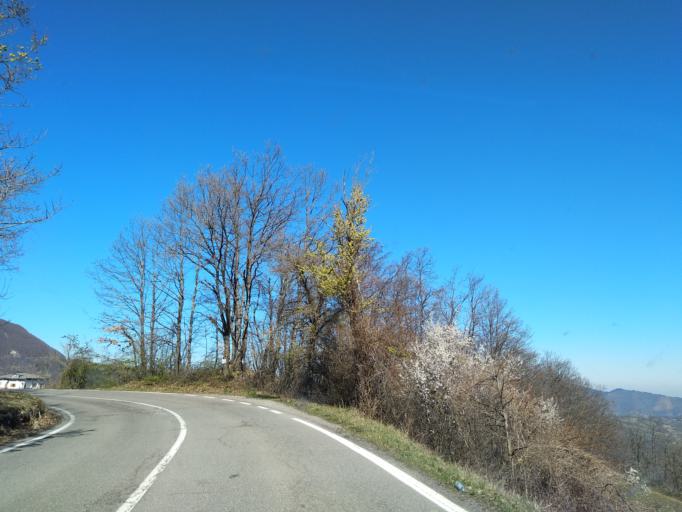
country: IT
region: Emilia-Romagna
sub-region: Provincia di Reggio Emilia
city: Ramiseto
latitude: 44.4147
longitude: 10.2896
